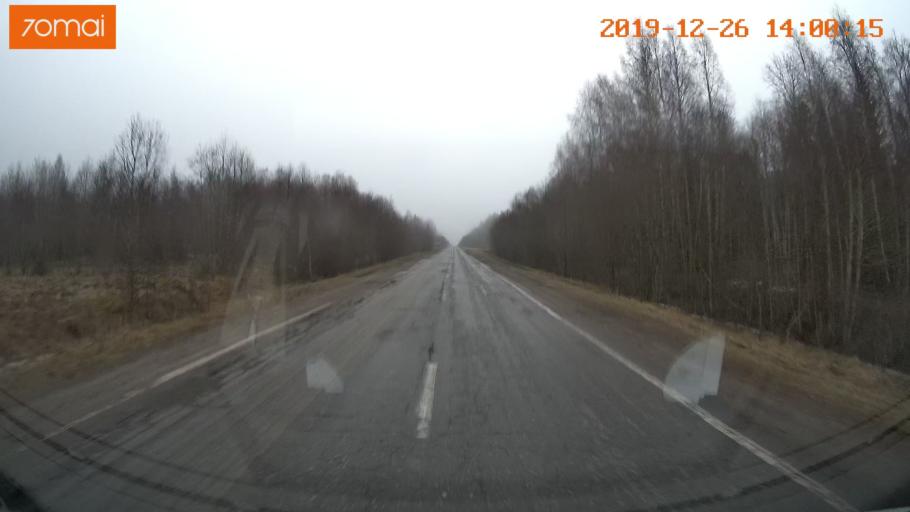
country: RU
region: Jaroslavl
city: Poshekhon'ye
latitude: 58.5595
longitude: 38.7396
